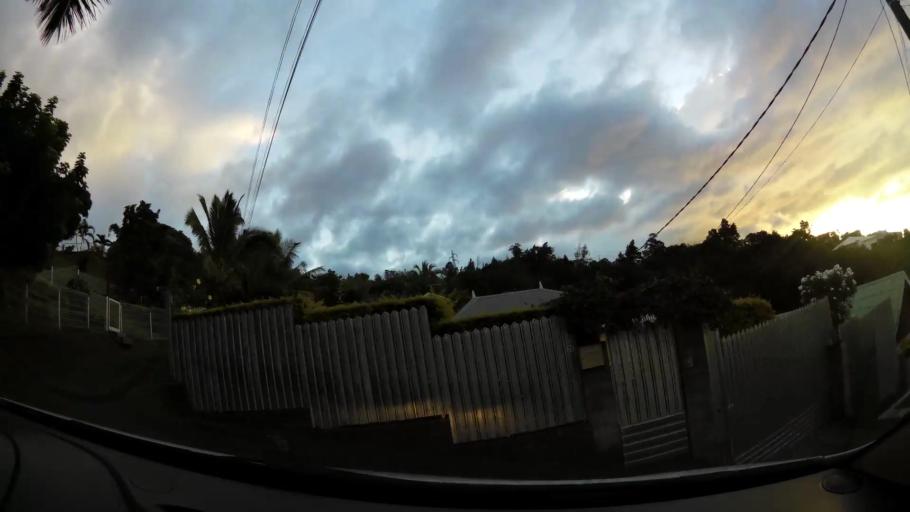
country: RE
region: Reunion
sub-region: Reunion
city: Saint-Denis
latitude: -20.9214
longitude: 55.4636
